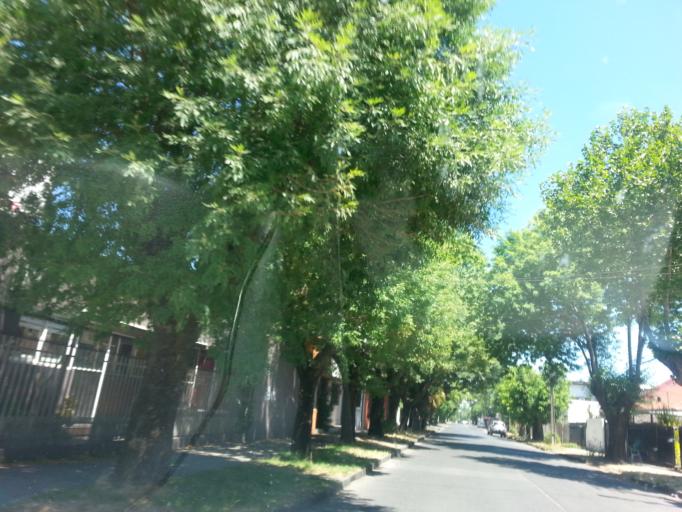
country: CL
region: Biobio
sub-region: Provincia de Nuble
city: Chillan
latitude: -36.6061
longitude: -72.0974
